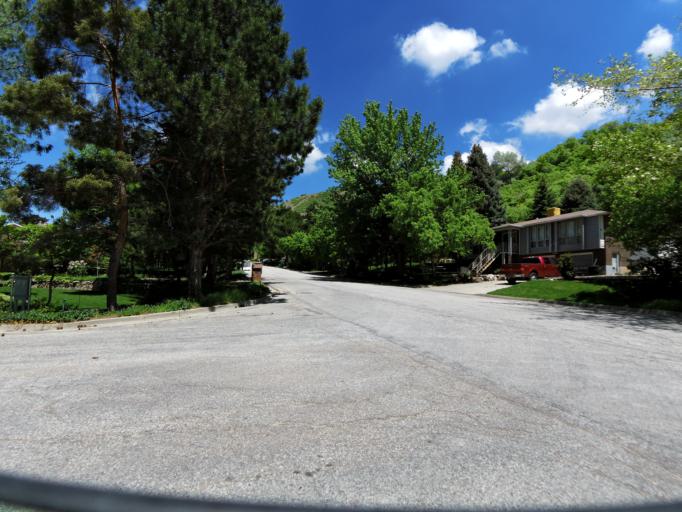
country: US
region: Utah
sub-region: Weber County
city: Uintah
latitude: 41.1598
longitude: -111.9187
